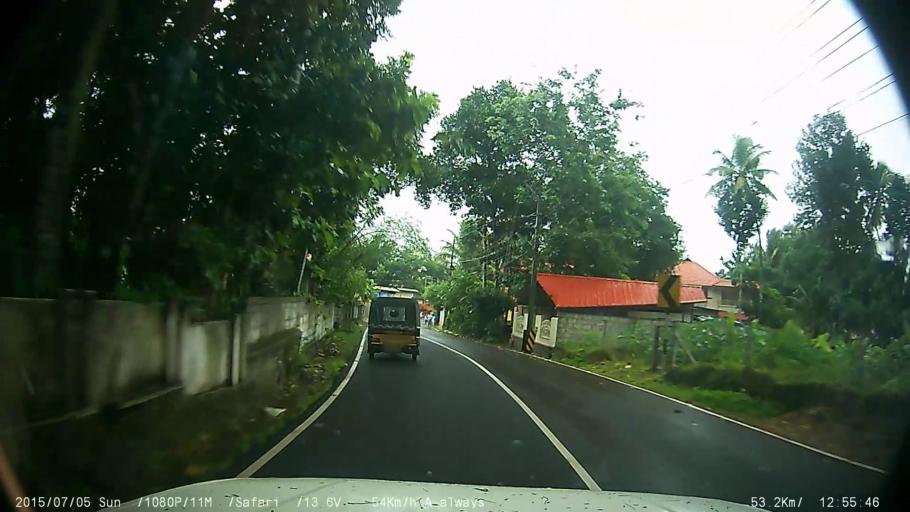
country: IN
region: Kerala
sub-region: Kottayam
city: Changanacheri
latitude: 9.4562
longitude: 76.5765
